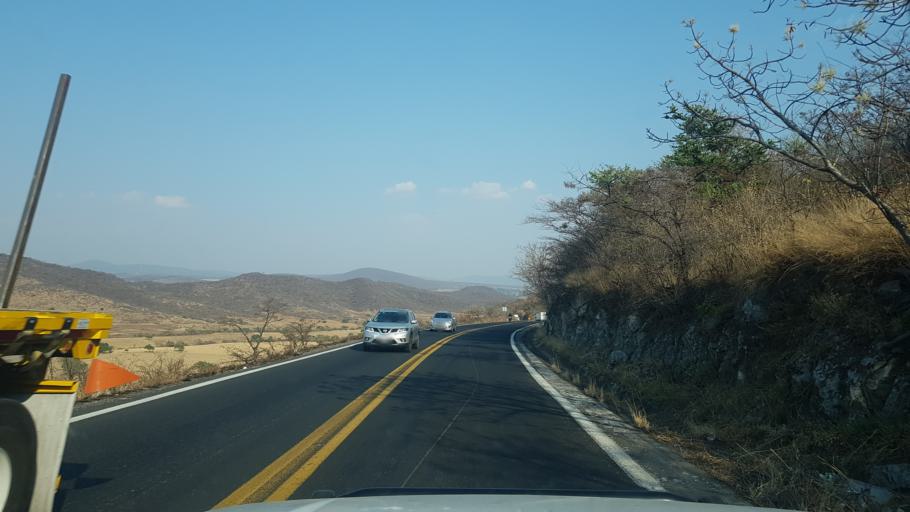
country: MX
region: Puebla
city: Calmeca
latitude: 18.6432
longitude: -98.5948
